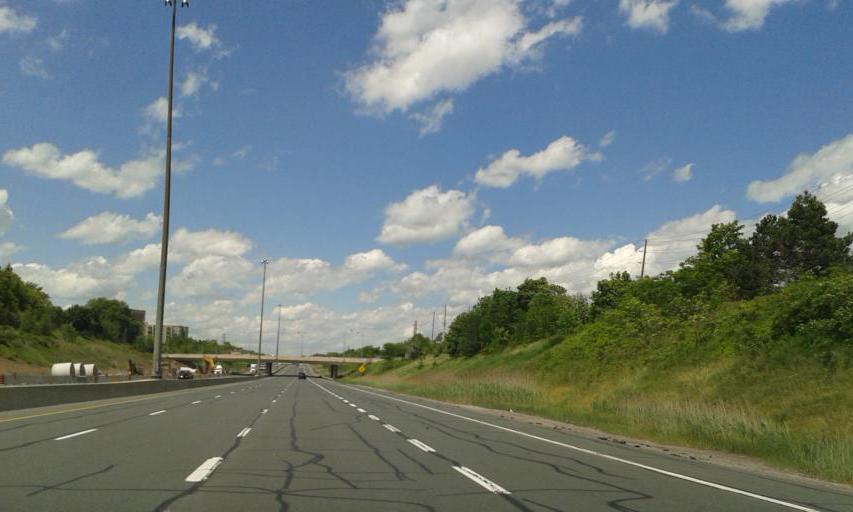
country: CA
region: Ontario
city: Burlington
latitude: 43.3447
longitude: -79.8310
